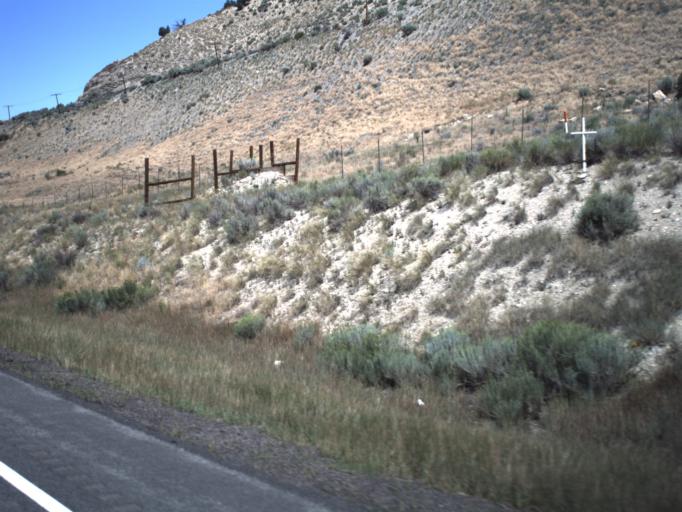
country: US
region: Utah
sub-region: Sanpete County
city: Fairview
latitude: 39.9295
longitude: -111.1931
